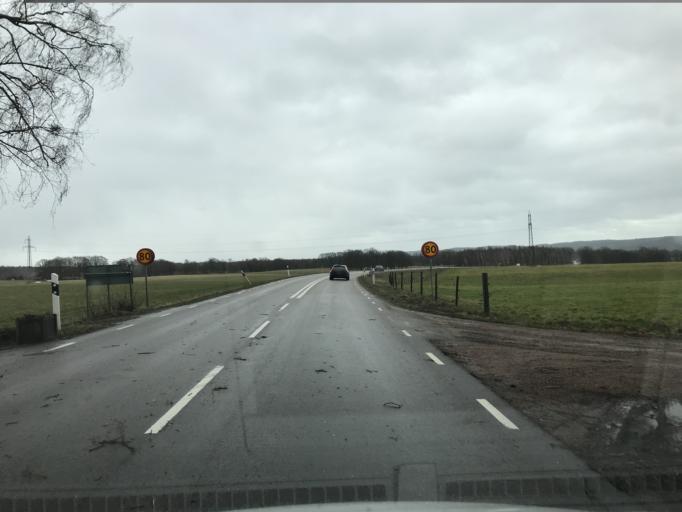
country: SE
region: Skane
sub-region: Klippans Kommun
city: Klippan
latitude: 56.1159
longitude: 13.1794
